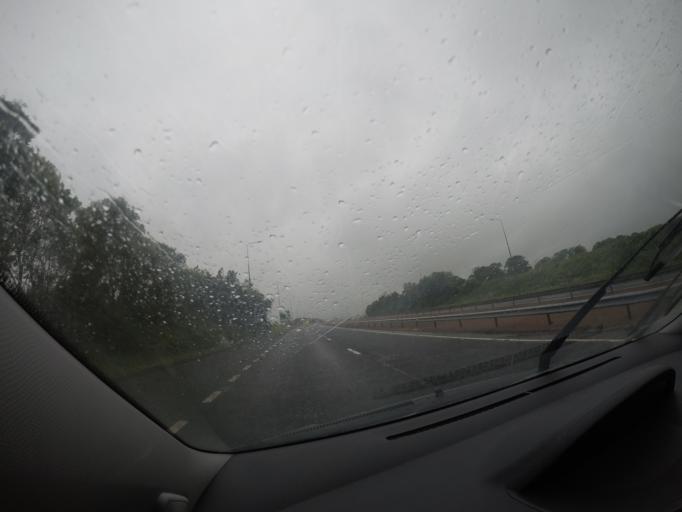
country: GB
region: Scotland
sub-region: Angus
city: Forfar
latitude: 56.5776
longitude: -2.9131
